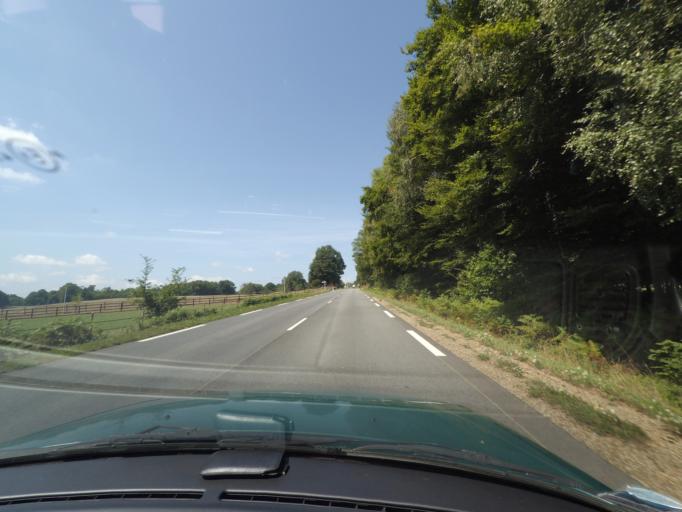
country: FR
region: Limousin
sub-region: Departement de la Haute-Vienne
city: Saint-Paul
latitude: 45.7958
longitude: 1.4315
